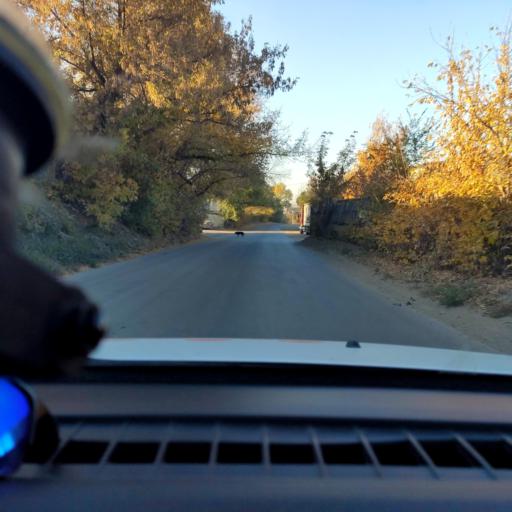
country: RU
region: Samara
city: Samara
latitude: 53.1776
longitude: 50.1553
